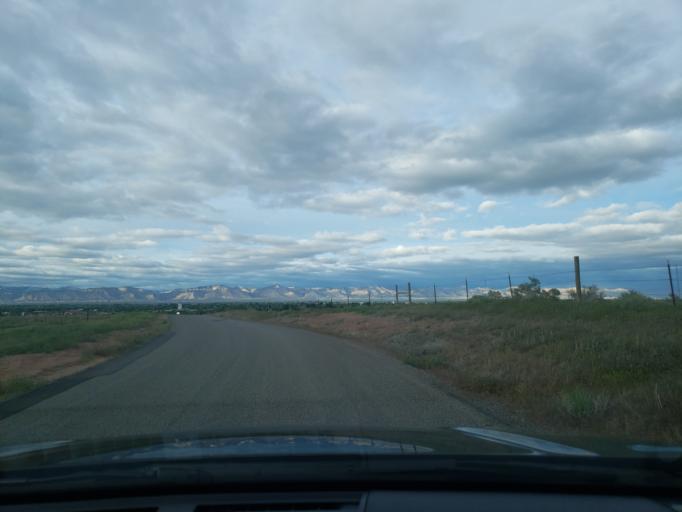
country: US
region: Colorado
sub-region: Mesa County
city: Fruita
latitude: 39.1405
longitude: -108.7495
